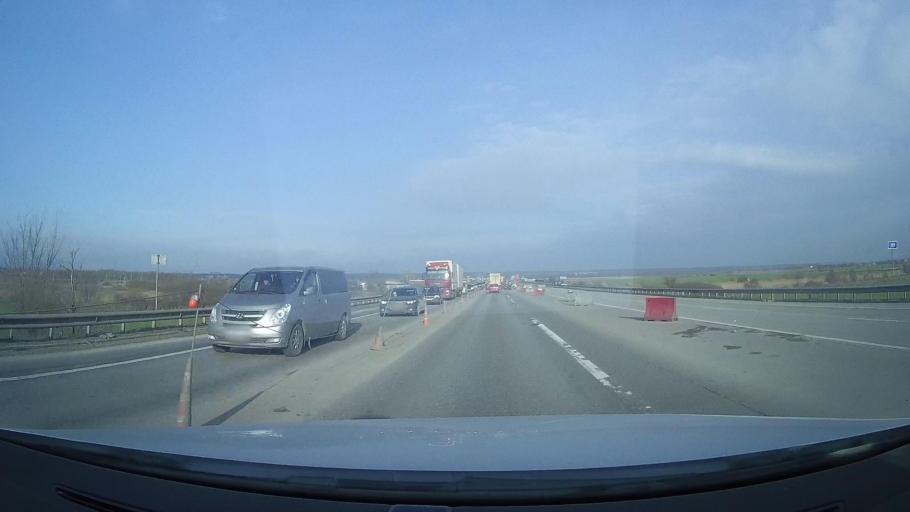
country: RU
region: Rostov
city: Grushevskaya
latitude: 47.4434
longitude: 39.9744
